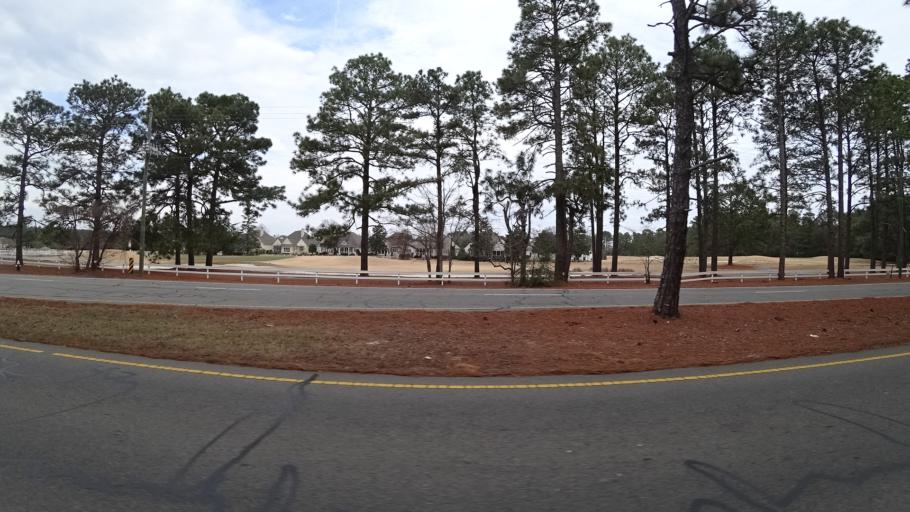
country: US
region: North Carolina
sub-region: Moore County
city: Southern Pines
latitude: 35.1996
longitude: -79.4206
